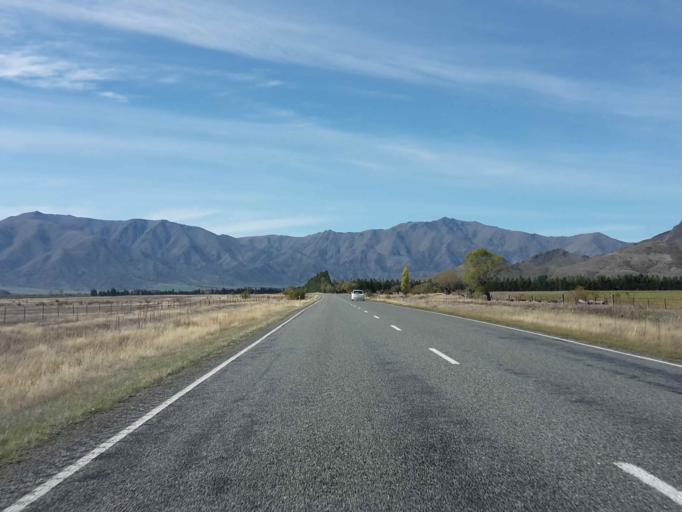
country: NZ
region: Otago
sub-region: Queenstown-Lakes District
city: Wanaka
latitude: -44.4964
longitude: 169.9156
